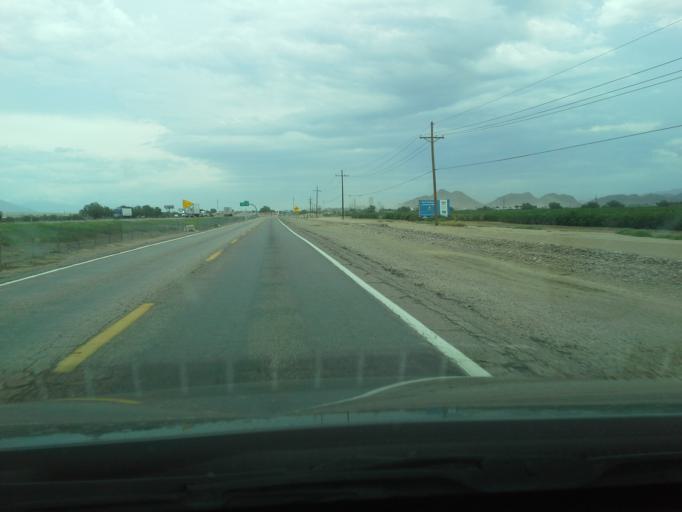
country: US
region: Arizona
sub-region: Pima County
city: Marana
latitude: 32.4299
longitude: -111.1718
